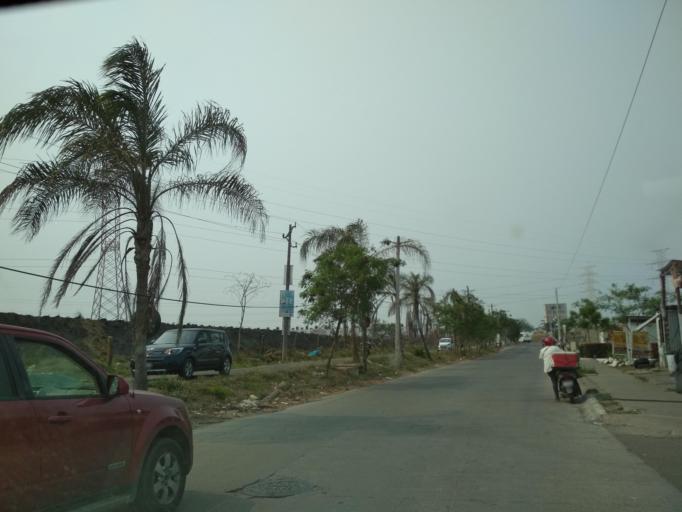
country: MX
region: Veracruz
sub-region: Veracruz
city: Las Amapolas
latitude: 19.1538
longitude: -96.2220
